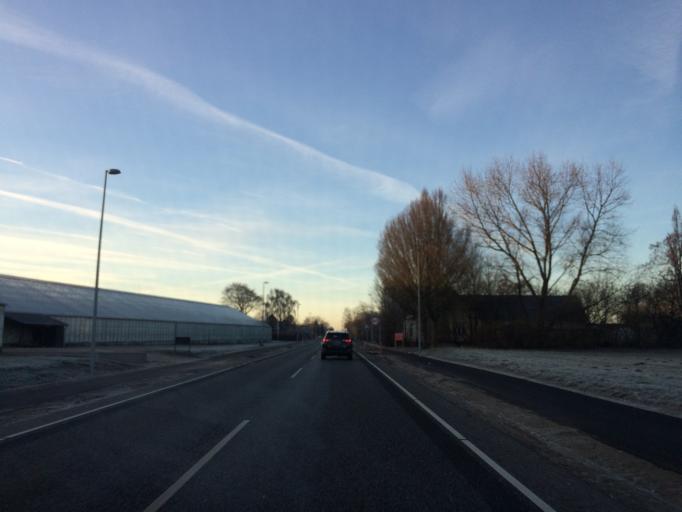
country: DK
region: South Denmark
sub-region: Odense Kommune
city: Bellinge
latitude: 55.3211
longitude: 10.3202
